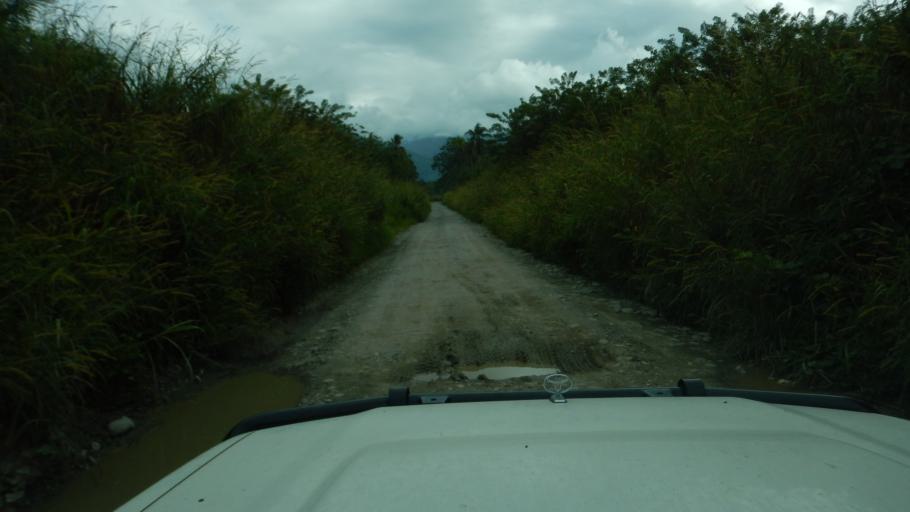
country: PG
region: Northern Province
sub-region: Sohe
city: Kokoda
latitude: -8.9104
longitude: 147.7949
